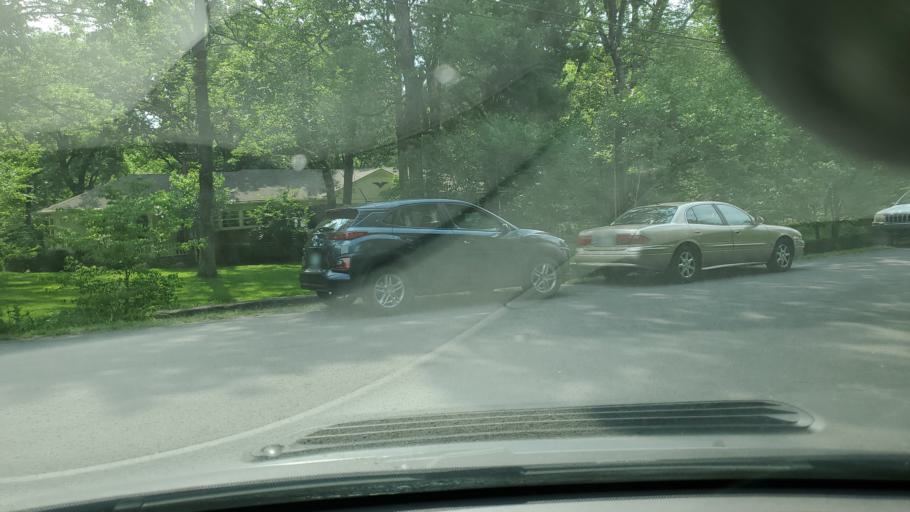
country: US
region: Tennessee
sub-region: Davidson County
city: Lakewood
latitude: 36.2287
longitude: -86.7179
